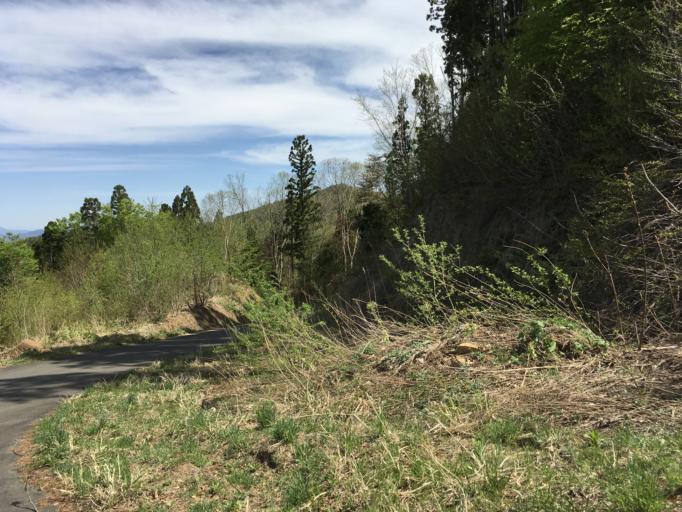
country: JP
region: Iwate
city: Mizusawa
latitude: 39.1151
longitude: 140.9191
